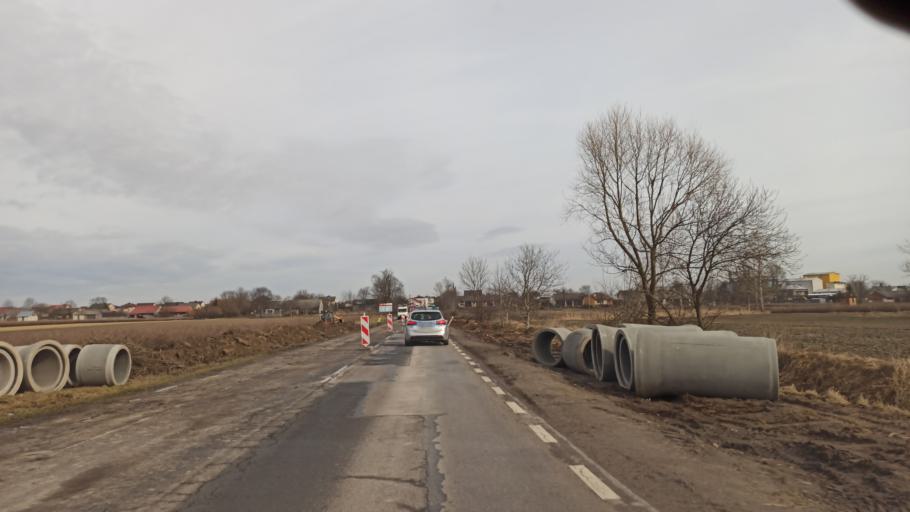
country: PL
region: Lublin Voivodeship
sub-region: Powiat bilgorajski
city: Tarnogrod
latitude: 50.3462
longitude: 22.7339
